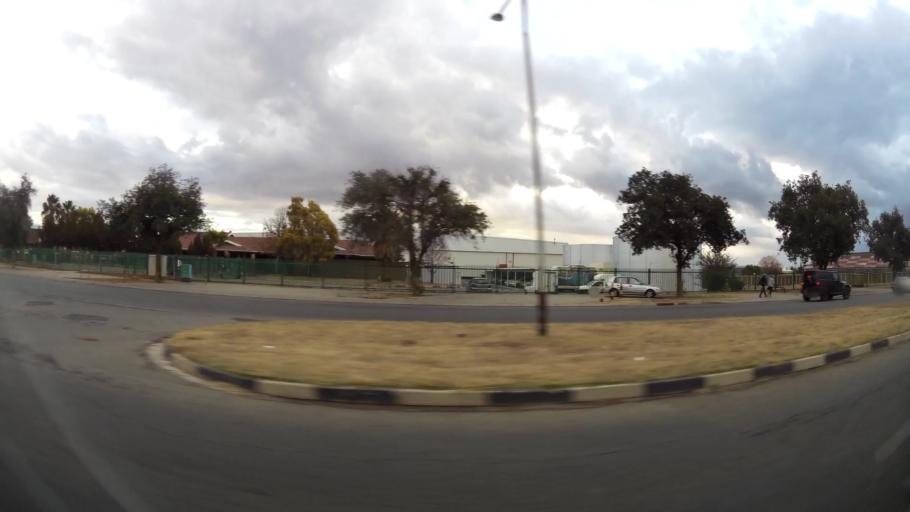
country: ZA
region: Orange Free State
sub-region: Lejweleputswa District Municipality
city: Welkom
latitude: -27.9707
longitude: 26.7519
